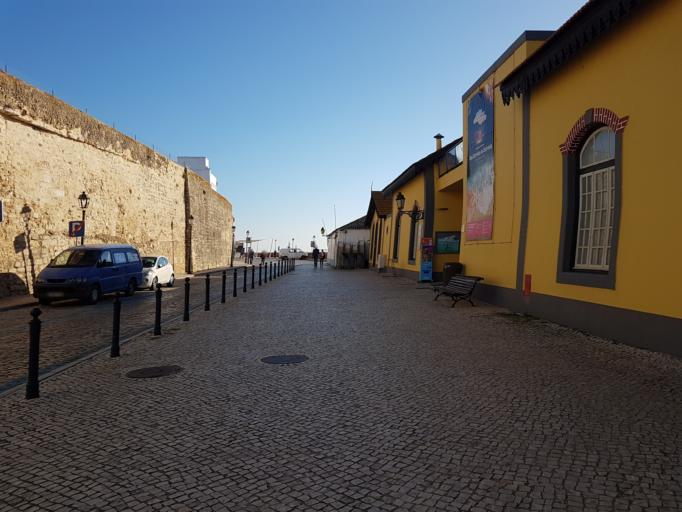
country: PT
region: Faro
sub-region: Faro
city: Faro
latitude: 37.0134
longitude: -7.9360
